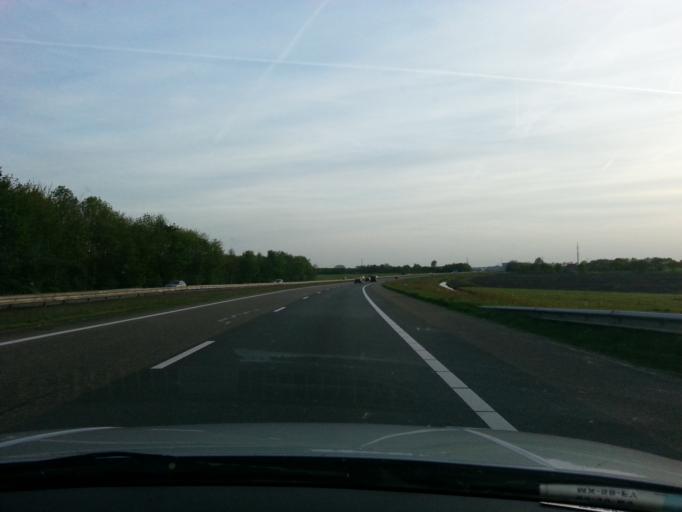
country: NL
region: Friesland
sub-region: Gemeente Heerenveen
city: De Knipe
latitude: 52.9931
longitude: 5.9858
